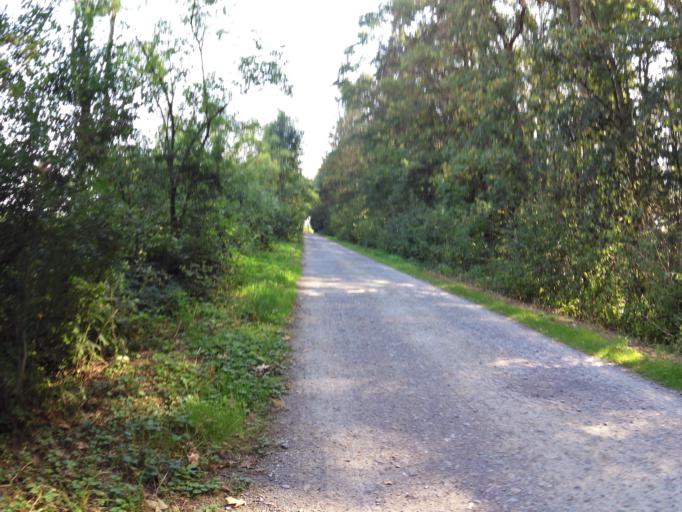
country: DE
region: North Rhine-Westphalia
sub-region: Regierungsbezirk Munster
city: Altenberge
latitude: 51.9739
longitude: 7.5131
